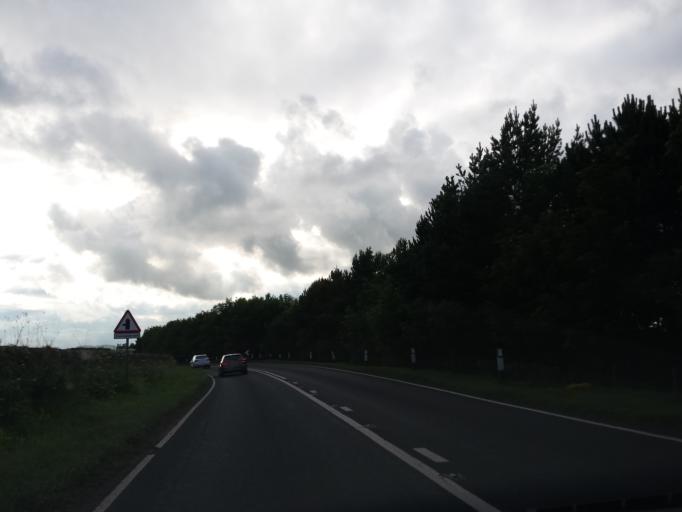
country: GB
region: Scotland
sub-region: Fife
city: Saint Andrews
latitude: 56.3497
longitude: -2.8336
